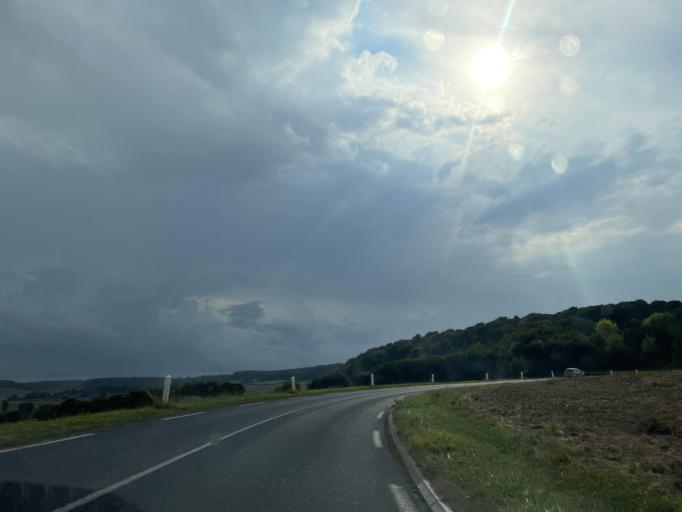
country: FR
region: Haute-Normandie
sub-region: Departement de la Seine-Maritime
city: Neufchatel-en-Bray
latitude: 49.7836
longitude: 1.4463
